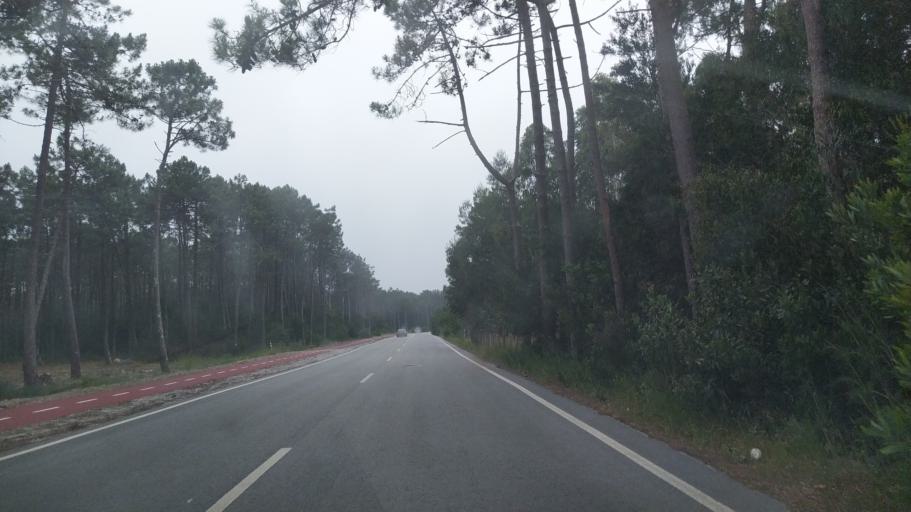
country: PT
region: Aveiro
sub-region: Ilhavo
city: Gafanha da Encarnacao
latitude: 40.5750
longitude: -8.7349
